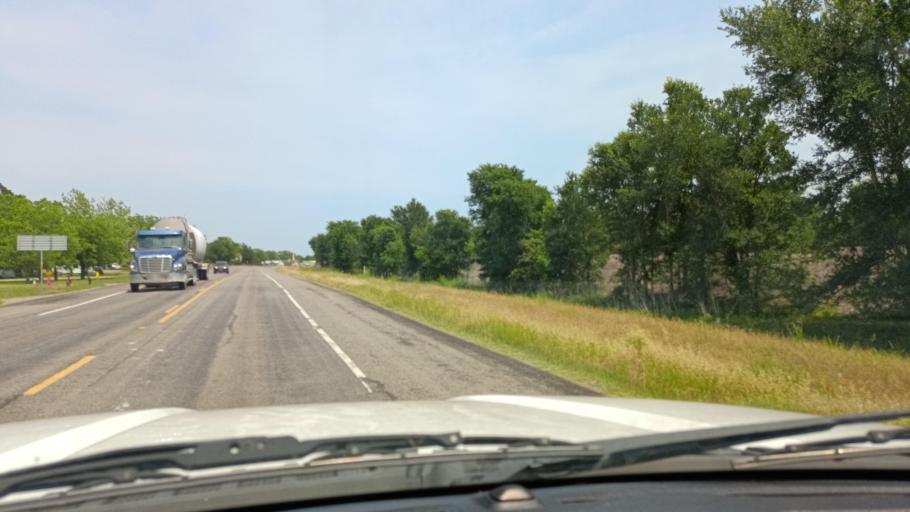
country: US
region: Texas
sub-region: Bell County
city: Rogers
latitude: 30.8753
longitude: -97.1314
